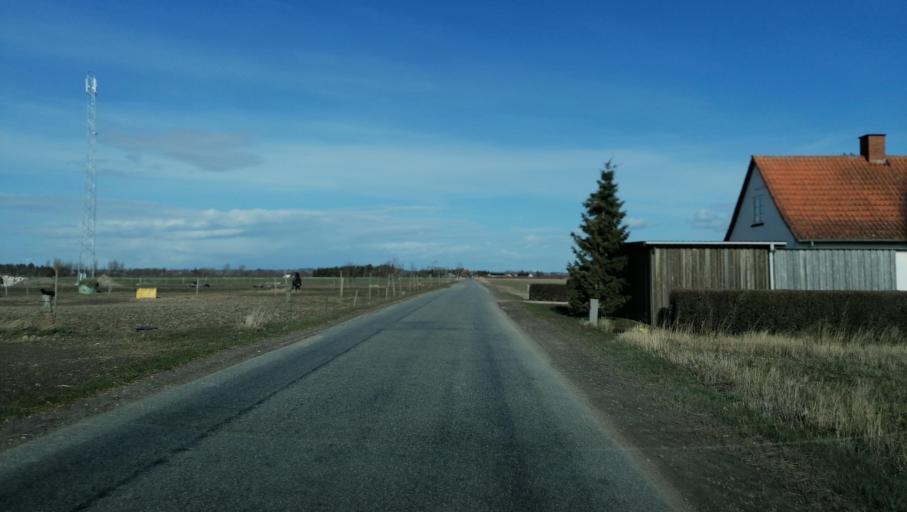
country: DK
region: Zealand
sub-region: Odsherred Kommune
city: Horve
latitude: 55.7594
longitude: 11.4982
